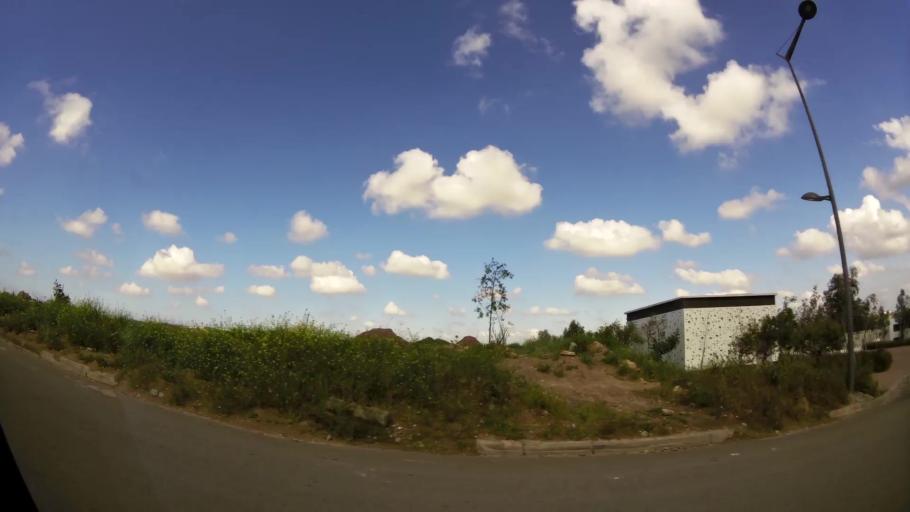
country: MA
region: Grand Casablanca
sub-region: Nouaceur
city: Bouskoura
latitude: 33.4798
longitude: -7.6229
